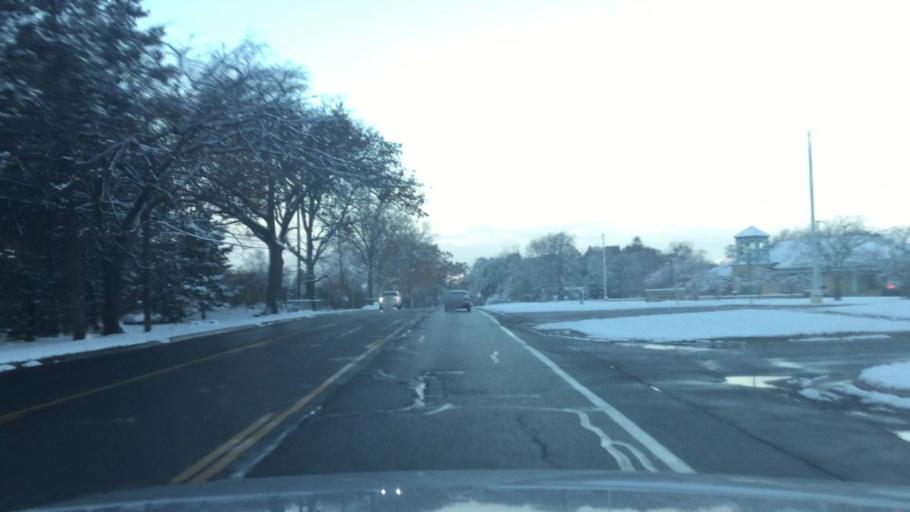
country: US
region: Michigan
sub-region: Oakland County
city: Wolverine Lake
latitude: 42.5923
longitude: -83.4501
